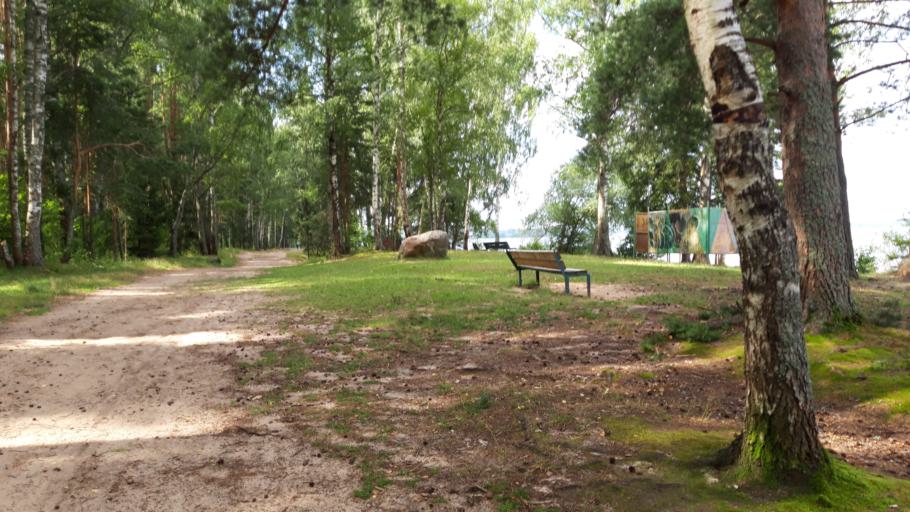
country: RU
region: Tverskaya
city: Konakovo
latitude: 56.6743
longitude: 36.6863
